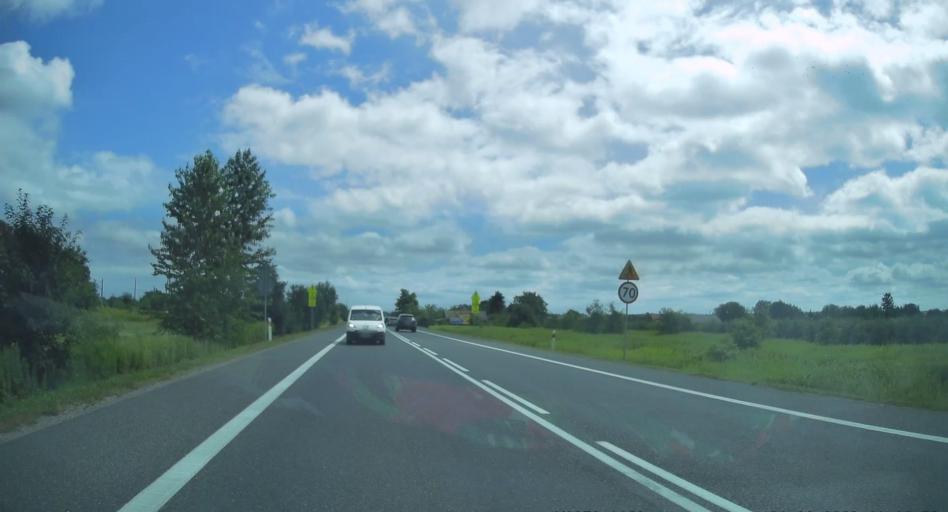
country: PL
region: Subcarpathian Voivodeship
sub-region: Powiat tarnobrzeski
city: Baranow Sandomierski
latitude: 50.5296
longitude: 21.5804
